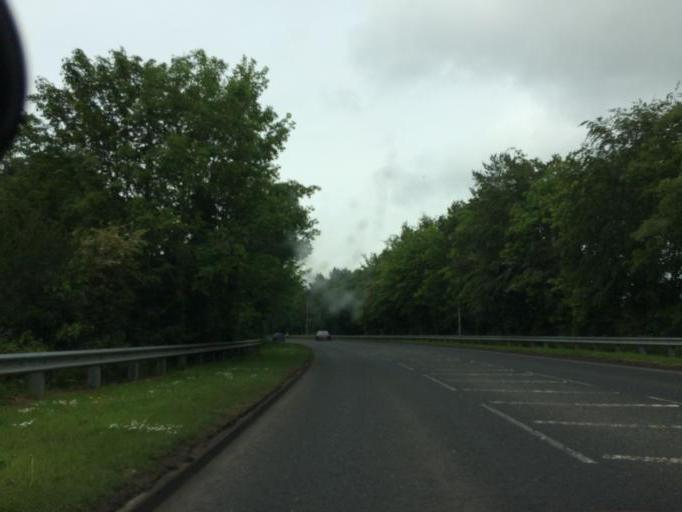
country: GB
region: Northern Ireland
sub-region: Antrim Borough
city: Antrim
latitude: 54.7101
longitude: -6.2195
